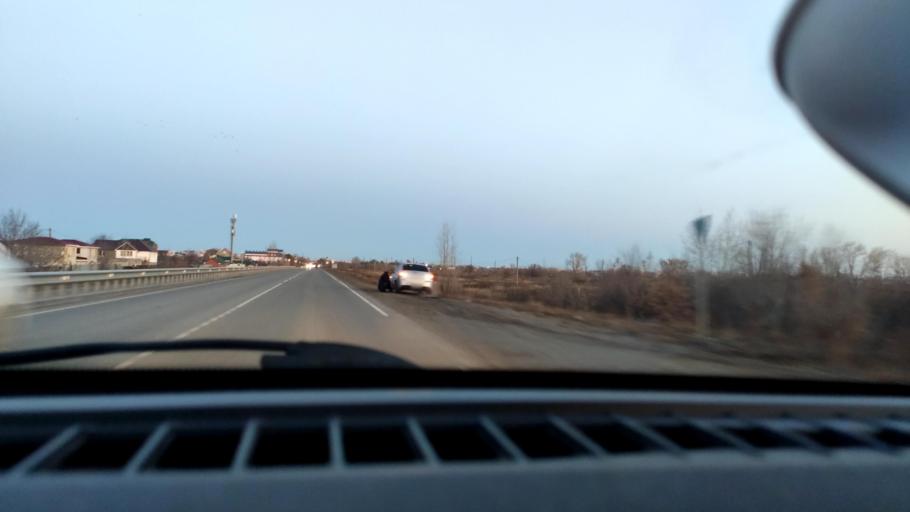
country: RU
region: Samara
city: Samara
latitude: 53.1200
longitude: 50.1198
